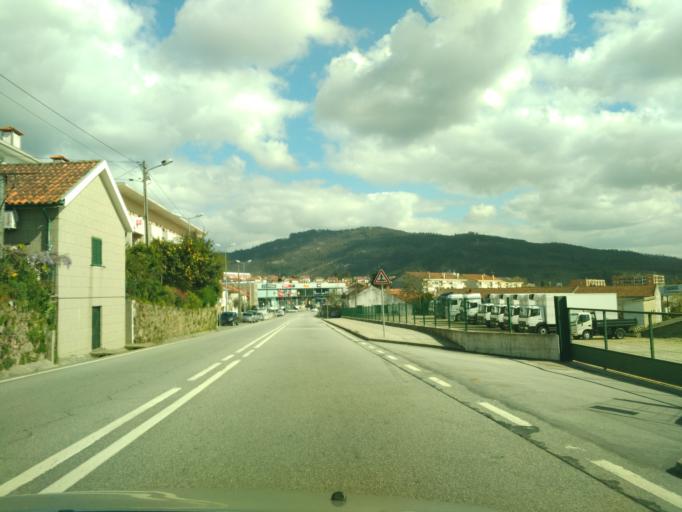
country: PT
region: Braga
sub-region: Braga
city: Braga
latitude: 41.5350
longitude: -8.4218
